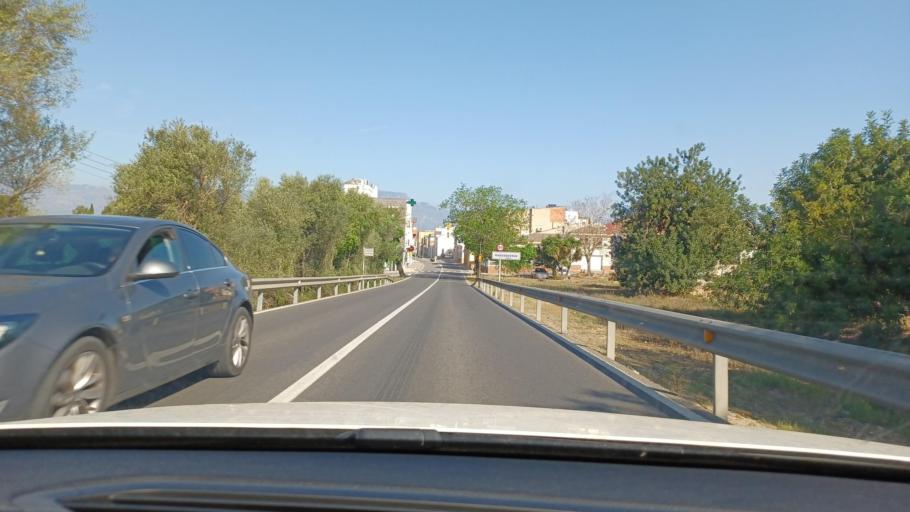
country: ES
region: Catalonia
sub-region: Provincia de Tarragona
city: Masdenverge
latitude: 40.7125
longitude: 0.5337
